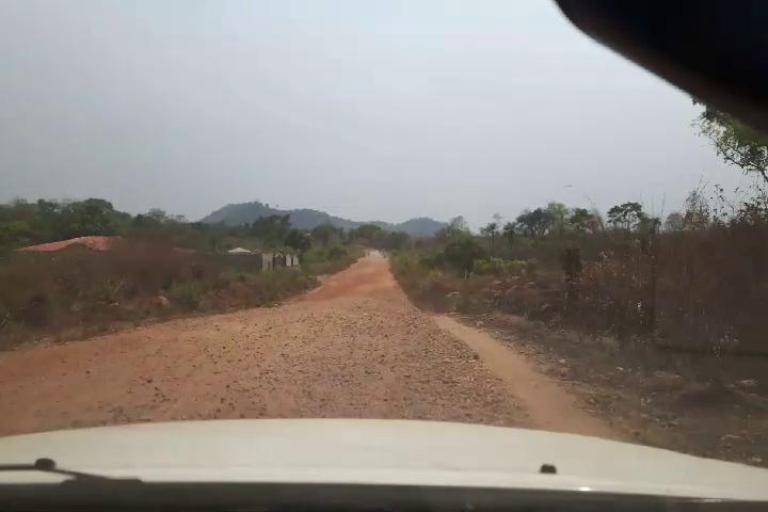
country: SL
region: Northern Province
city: Bumbuna
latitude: 9.0353
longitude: -11.7607
